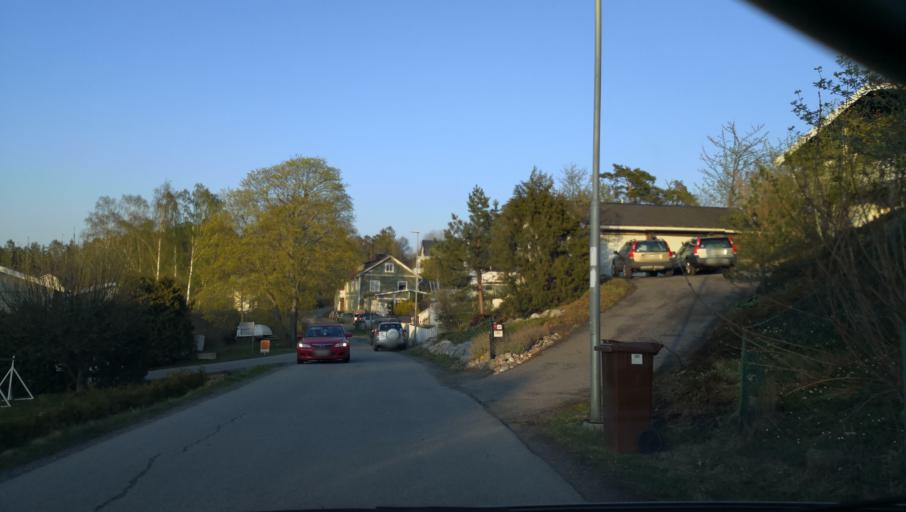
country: SE
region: Stockholm
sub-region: Varmdo Kommun
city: Mortnas
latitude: 59.3195
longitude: 18.4719
